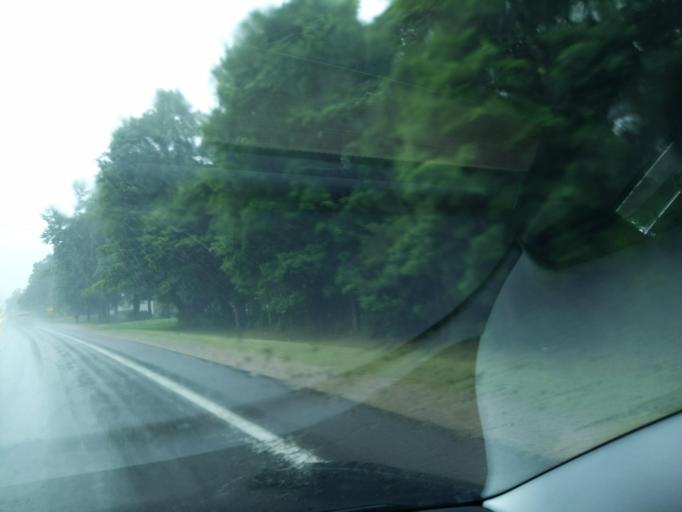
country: US
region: Michigan
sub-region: Muskegon County
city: Fruitport
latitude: 43.1489
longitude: -86.1613
